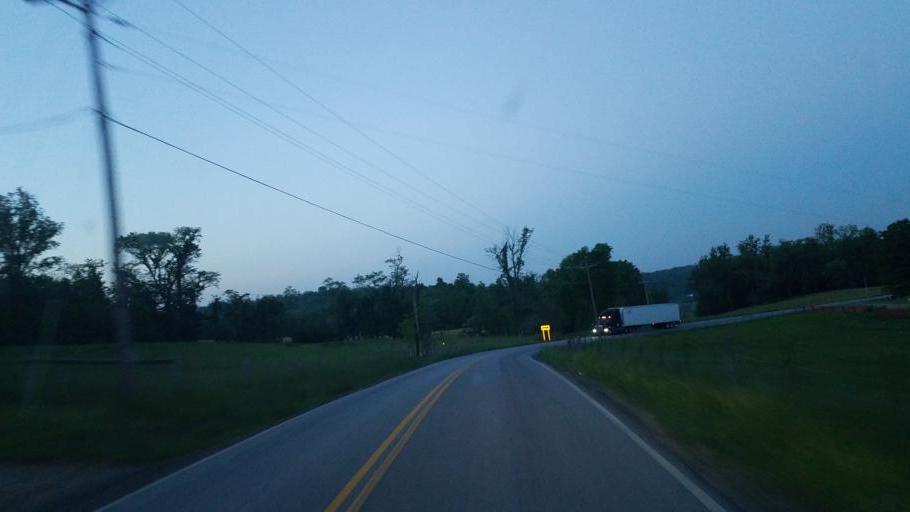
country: US
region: Ohio
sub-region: Belmont County
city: Barnesville
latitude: 40.0846
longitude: -81.3193
